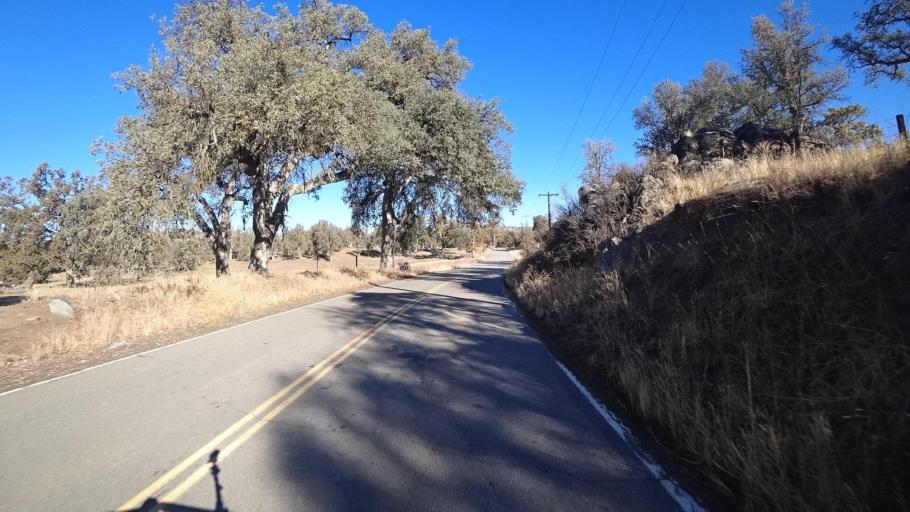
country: US
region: California
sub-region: Kern County
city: Alta Sierra
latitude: 35.7617
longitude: -118.7122
